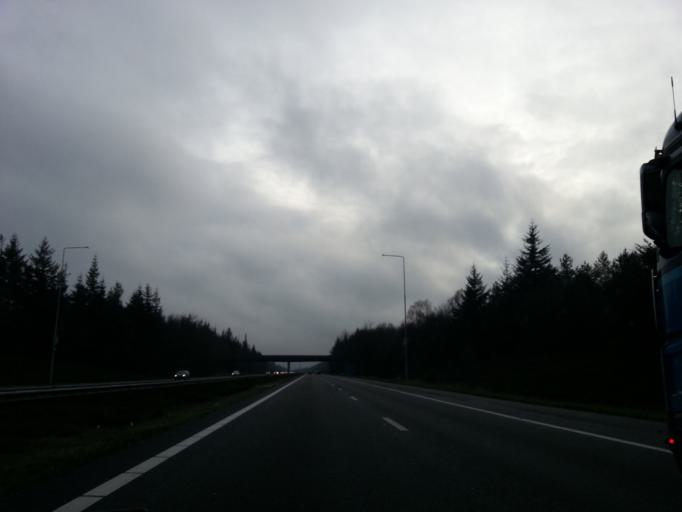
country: NL
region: Gelderland
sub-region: Gemeente Heerde
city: Heerde
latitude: 52.4276
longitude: 6.0177
